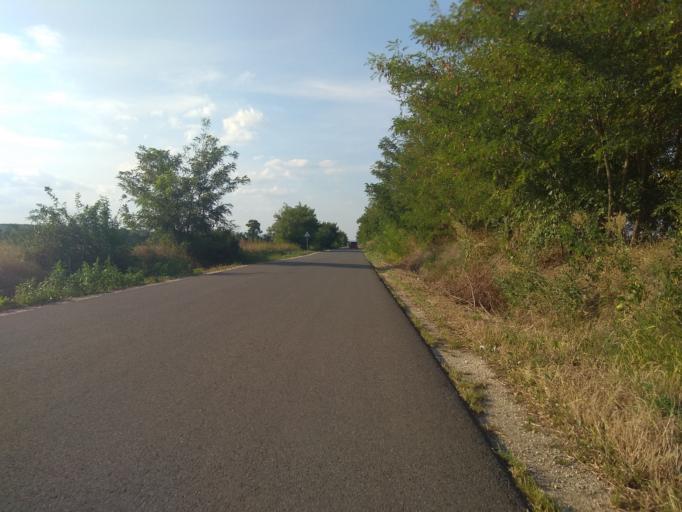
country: HU
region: Borsod-Abauj-Zemplen
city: Harsany
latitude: 47.9000
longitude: 20.7453
